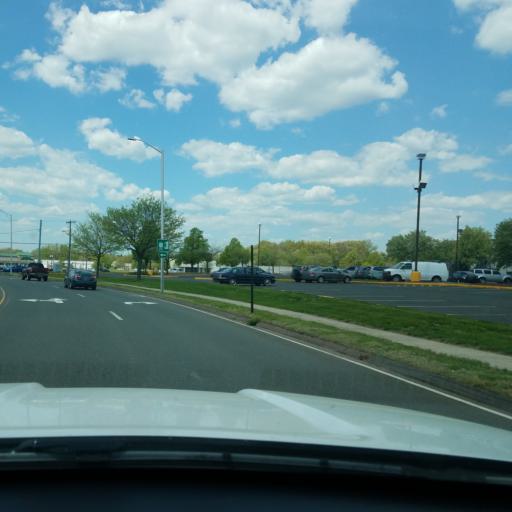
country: US
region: Connecticut
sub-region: Hartford County
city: Kensington
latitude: 41.6290
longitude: -72.7439
